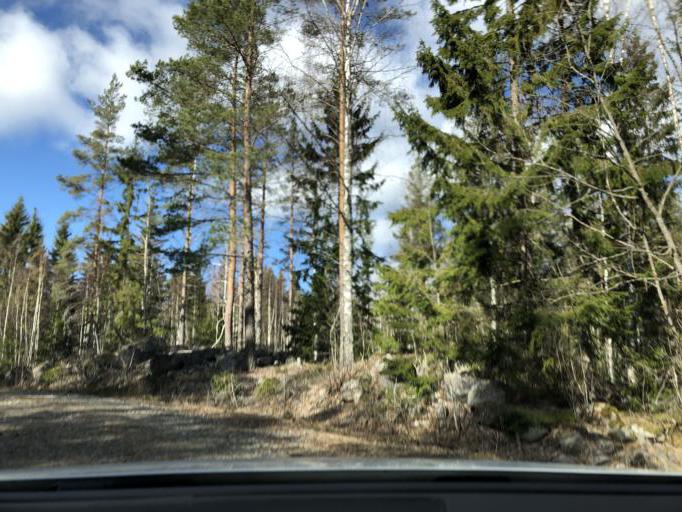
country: SE
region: Uppsala
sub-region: Heby Kommun
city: Tarnsjo
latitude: 60.3015
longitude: 16.8504
